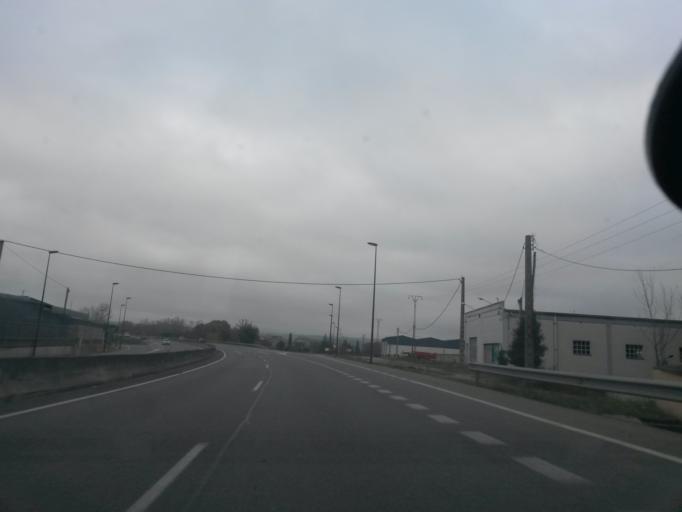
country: ES
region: Catalonia
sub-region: Provincia de Girona
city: Cornella del Terri
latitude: 42.0812
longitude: 2.8180
